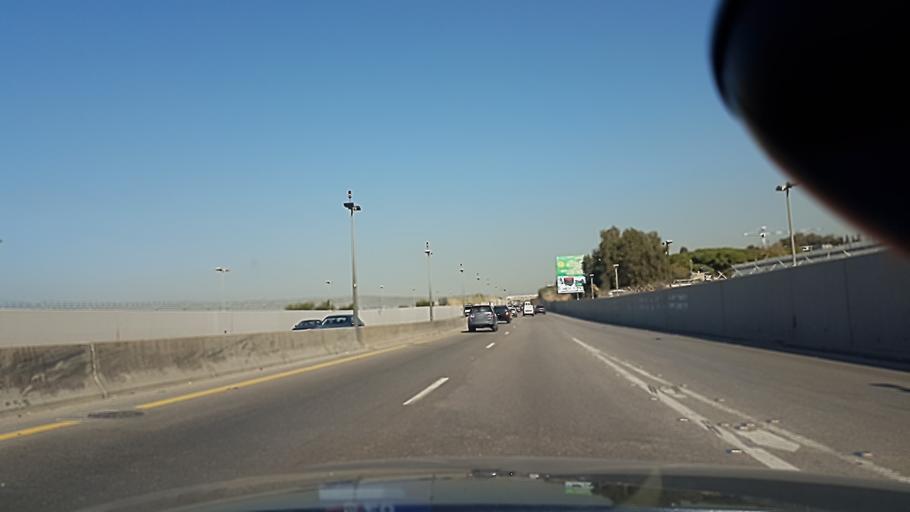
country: LB
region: Mont-Liban
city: Baabda
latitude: 33.7976
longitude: 35.4828
